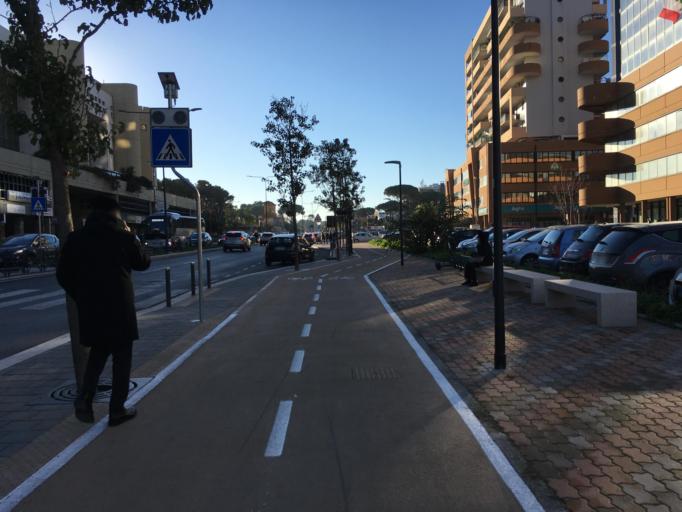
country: IT
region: Apulia
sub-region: Provincia di Bari
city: Bari
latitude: 41.1018
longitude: 16.8878
